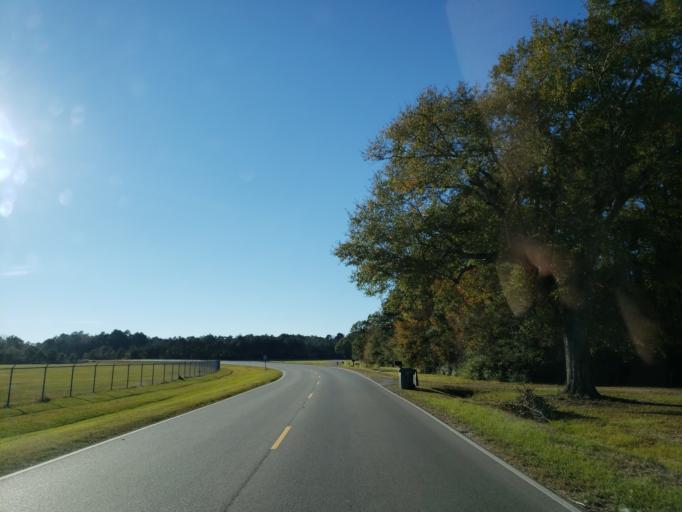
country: US
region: Mississippi
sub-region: Forrest County
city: Hattiesburg
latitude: 31.2732
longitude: -89.2590
